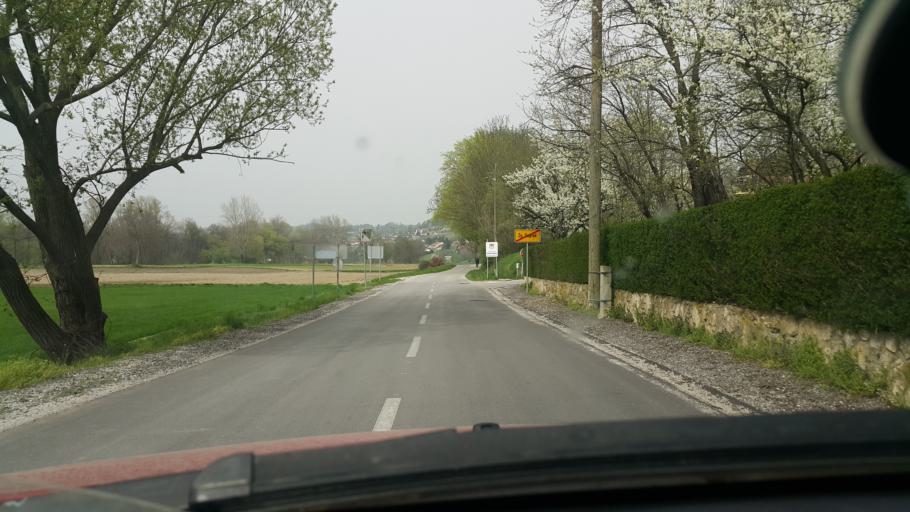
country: SI
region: Duplek
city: Zgornji Duplek
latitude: 46.5272
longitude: 15.7167
